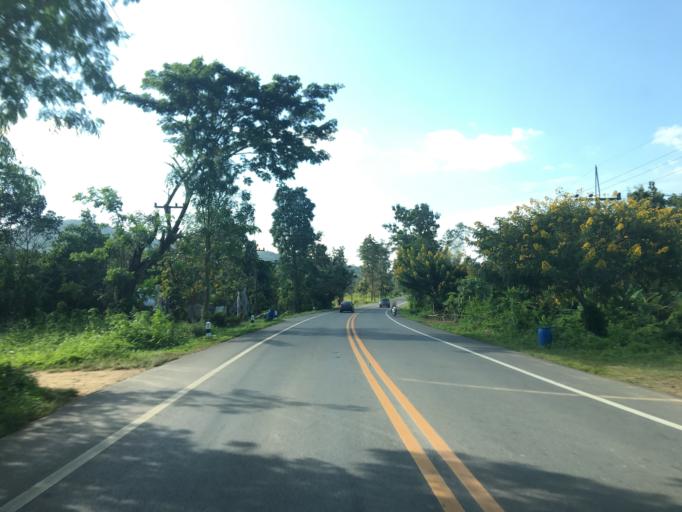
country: TH
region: Phayao
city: Chun
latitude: 19.3517
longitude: 100.1045
